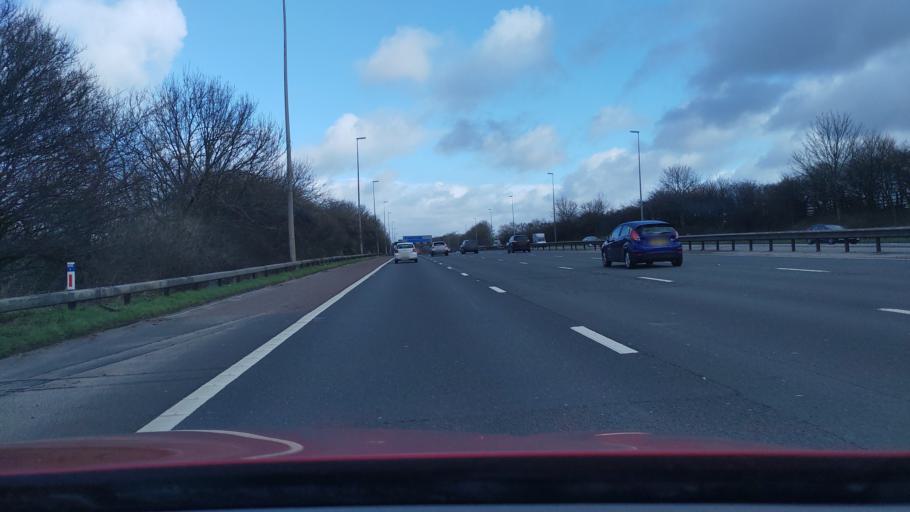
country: GB
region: England
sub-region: Lancashire
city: Clayton-le-Woods
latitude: 53.7506
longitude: -2.6441
